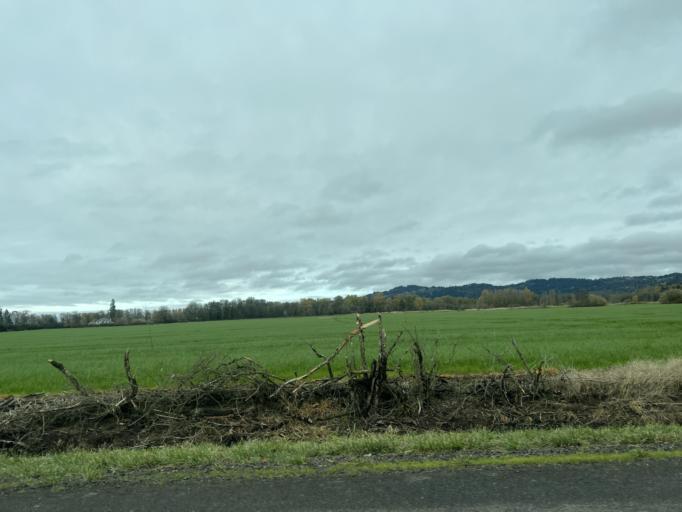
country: US
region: Oregon
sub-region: Marion County
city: Jefferson
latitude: 44.7922
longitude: -123.0927
